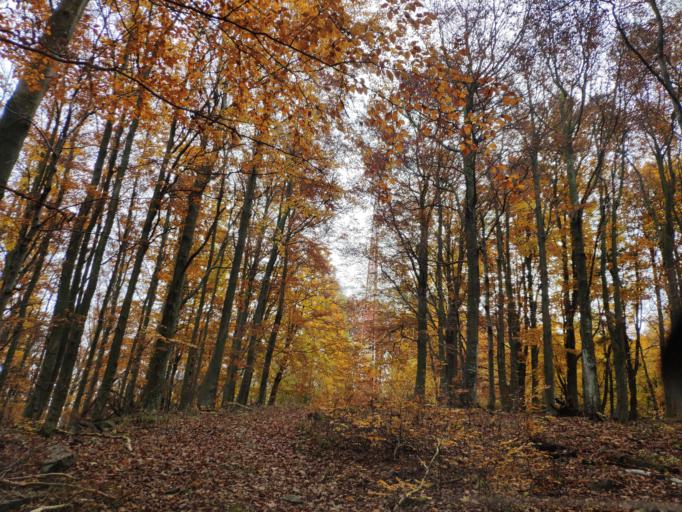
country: SK
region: Kosicky
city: Medzev
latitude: 48.7351
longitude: 21.0047
